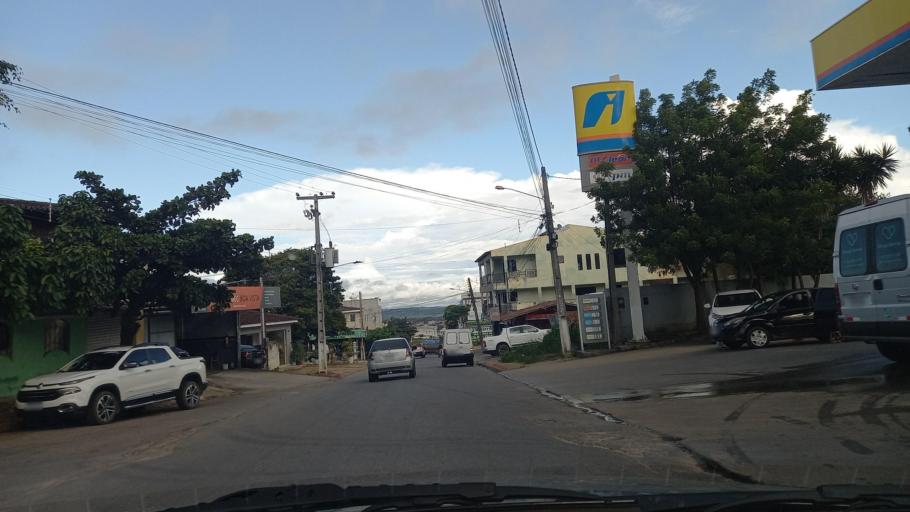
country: BR
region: Pernambuco
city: Garanhuns
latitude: -8.9058
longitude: -36.4894
